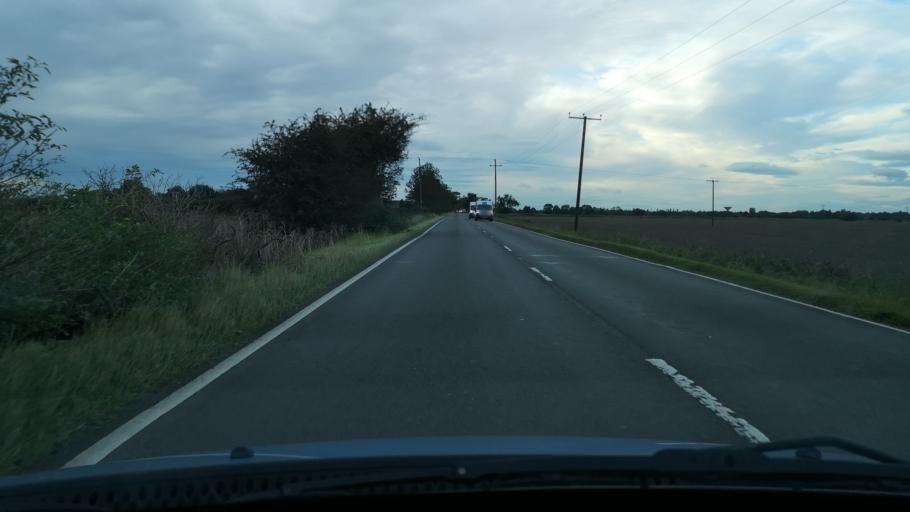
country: GB
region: England
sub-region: Doncaster
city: Hatfield
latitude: 53.5911
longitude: -0.9343
